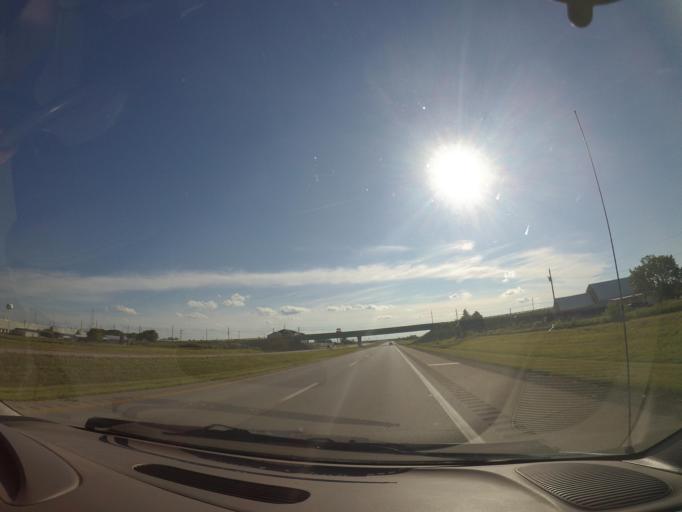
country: US
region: Ohio
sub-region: Henry County
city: Napoleon
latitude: 41.4162
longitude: -84.0940
